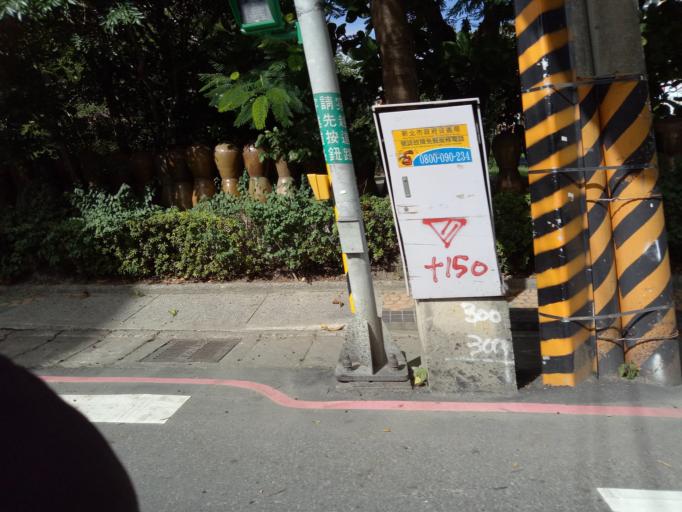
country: TW
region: Taiwan
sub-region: Taoyuan
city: Taoyuan
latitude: 24.9403
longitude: 121.3370
